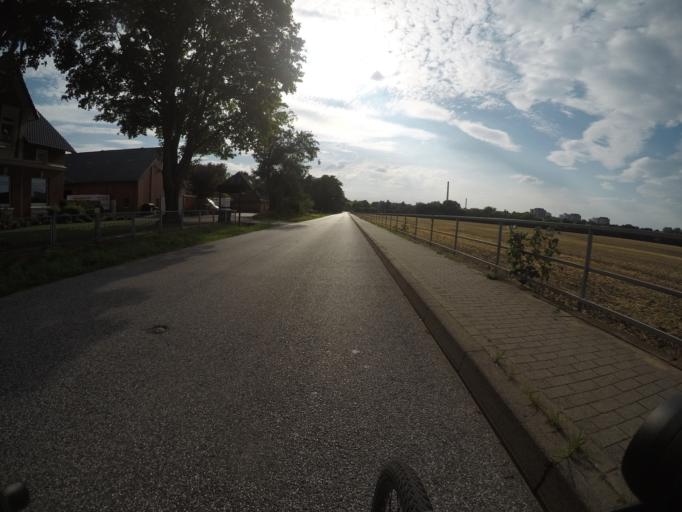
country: DE
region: Schleswig-Holstein
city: Oststeinbek
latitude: 53.5230
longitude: 10.1610
